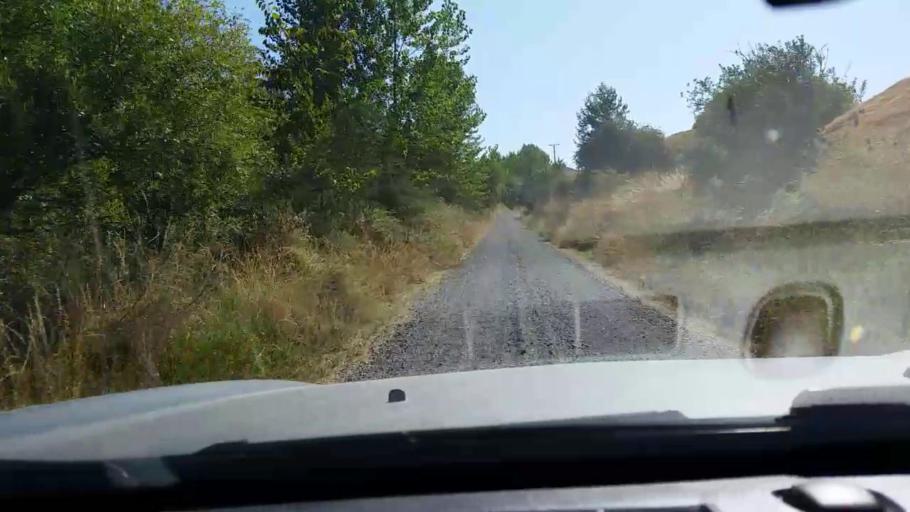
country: NZ
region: Bay of Plenty
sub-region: Rotorua District
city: Rotorua
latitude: -38.2995
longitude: 176.2752
